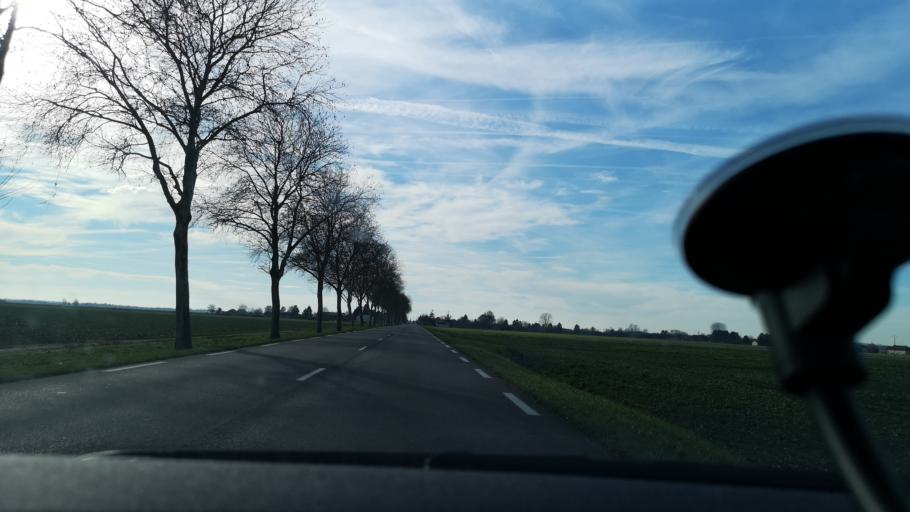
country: FR
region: Franche-Comte
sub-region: Departement du Jura
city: Saint-Aubin
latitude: 46.9862
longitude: 5.3272
